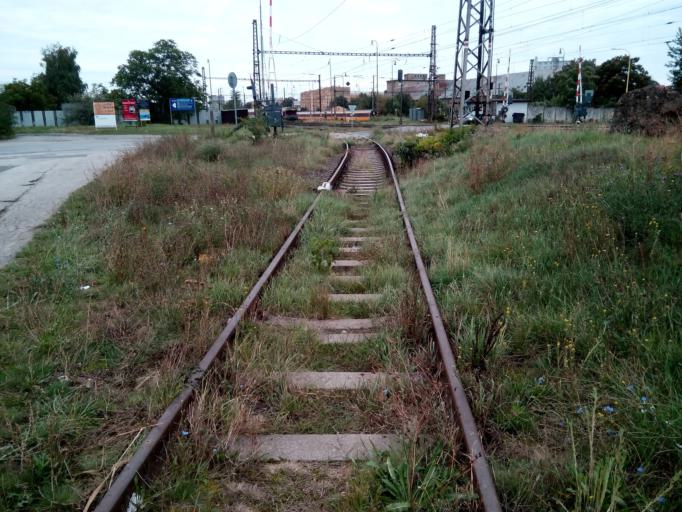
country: SK
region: Kosicky
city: Kosice
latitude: 48.7347
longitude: 21.2631
